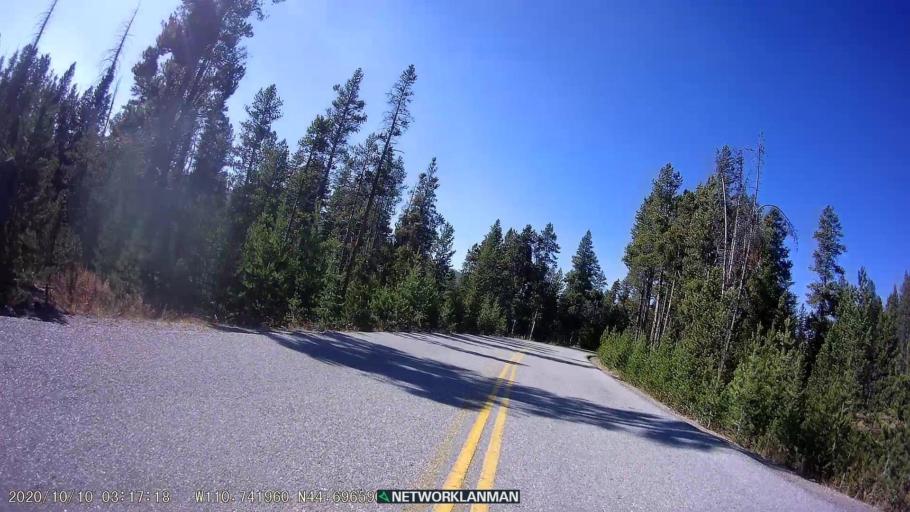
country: US
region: Montana
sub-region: Gallatin County
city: West Yellowstone
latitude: 44.6968
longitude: -110.7420
